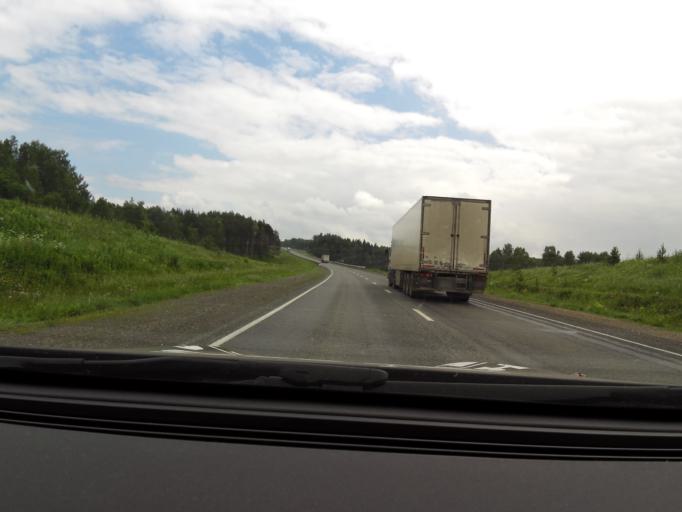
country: RU
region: Perm
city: Suksun
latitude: 57.0979
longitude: 57.3152
